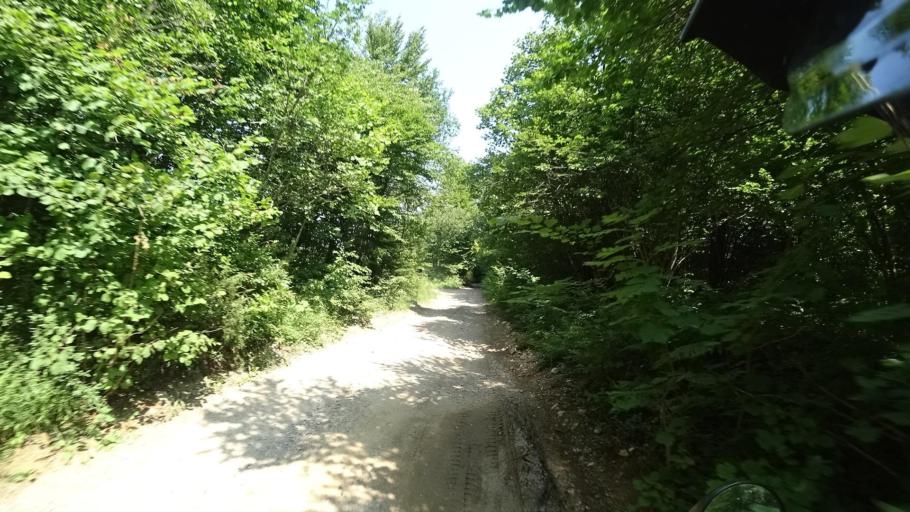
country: HR
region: Primorsko-Goranska
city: Vrbovsko
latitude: 45.3054
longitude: 15.1382
